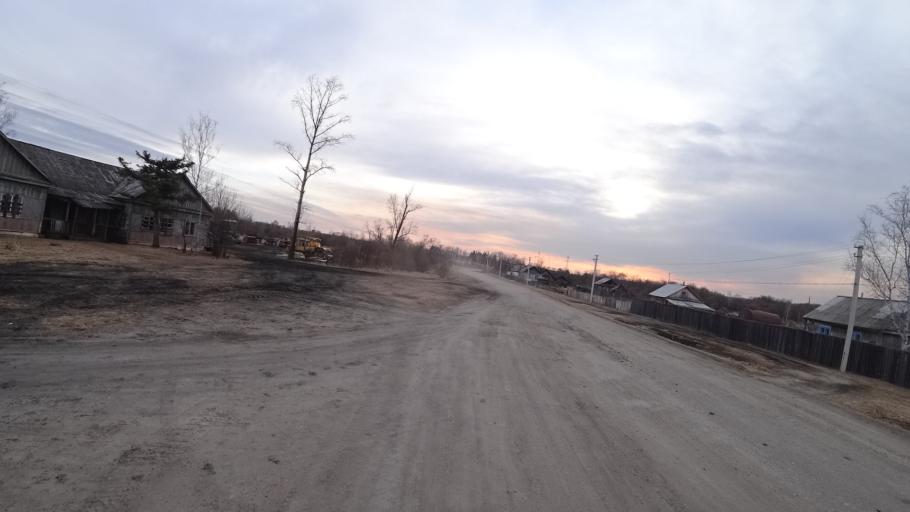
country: RU
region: Amur
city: Bureya
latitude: 50.0210
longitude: 129.7766
